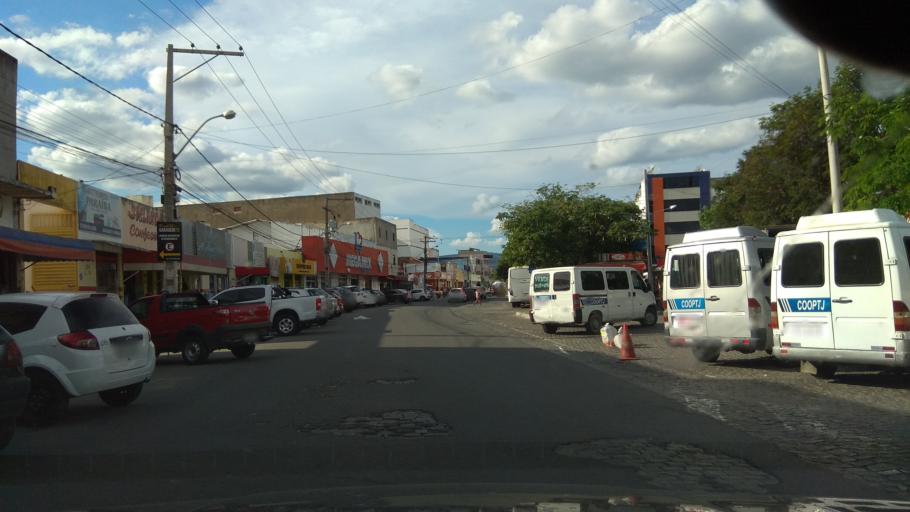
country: BR
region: Bahia
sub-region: Jequie
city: Jequie
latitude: -13.8618
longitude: -40.0791
